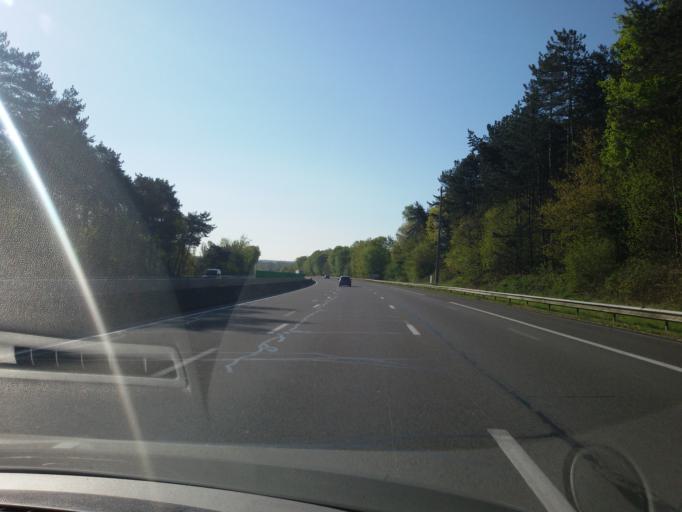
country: FR
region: Ile-de-France
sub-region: Departement de Seine-et-Marne
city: Nemours
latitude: 48.2941
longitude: 2.6742
